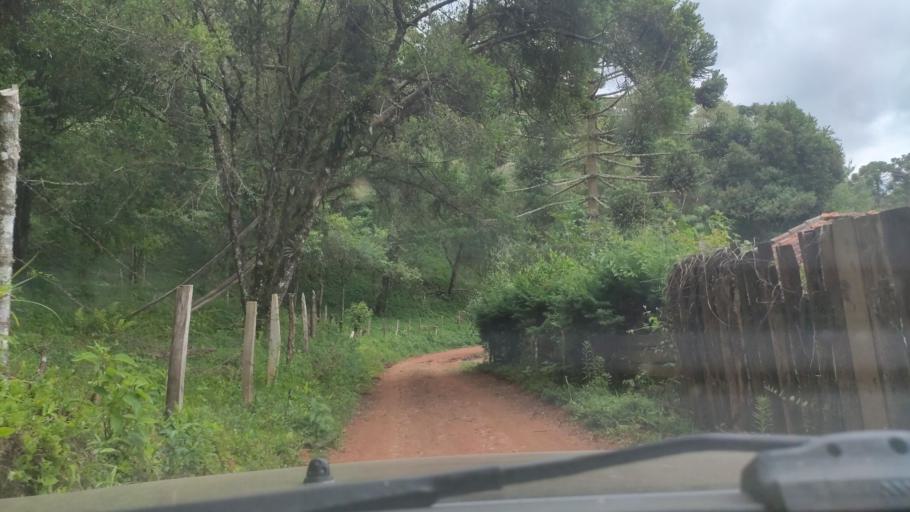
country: BR
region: Minas Gerais
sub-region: Paraisopolis
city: Paraisopolis
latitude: -22.7242
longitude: -45.8314
